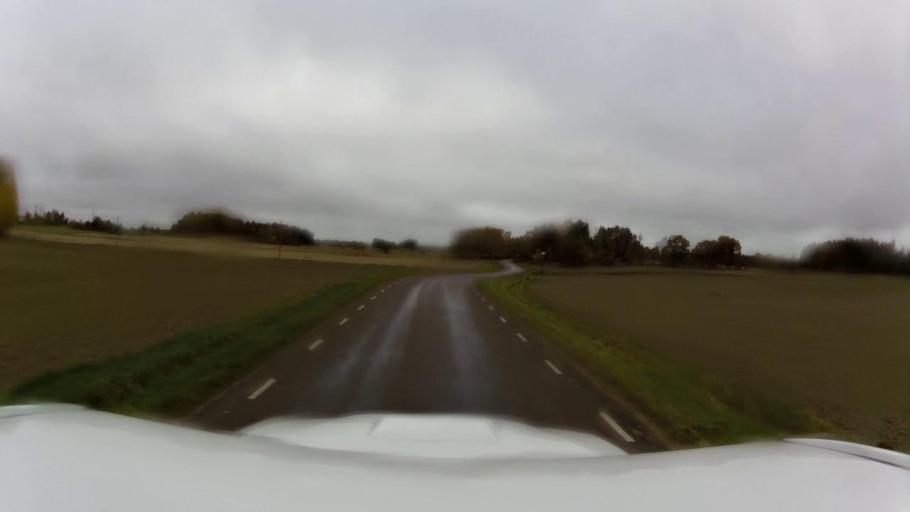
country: SE
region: OEstergoetland
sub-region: Linkopings Kommun
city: Linghem
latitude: 58.4585
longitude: 15.8294
